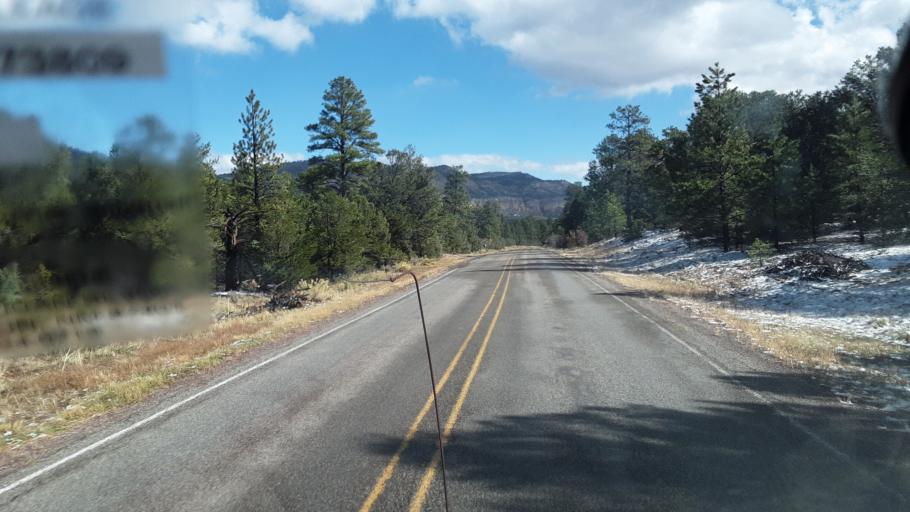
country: US
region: New Mexico
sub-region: Rio Arriba County
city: Santa Teresa
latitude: 36.2019
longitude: -106.7276
